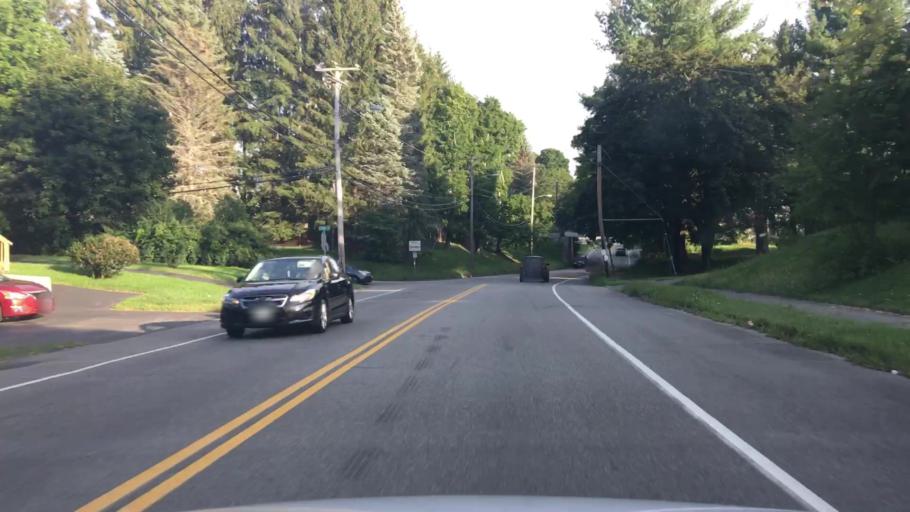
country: US
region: Maine
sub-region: Cumberland County
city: Westbrook
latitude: 43.6869
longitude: -70.3582
